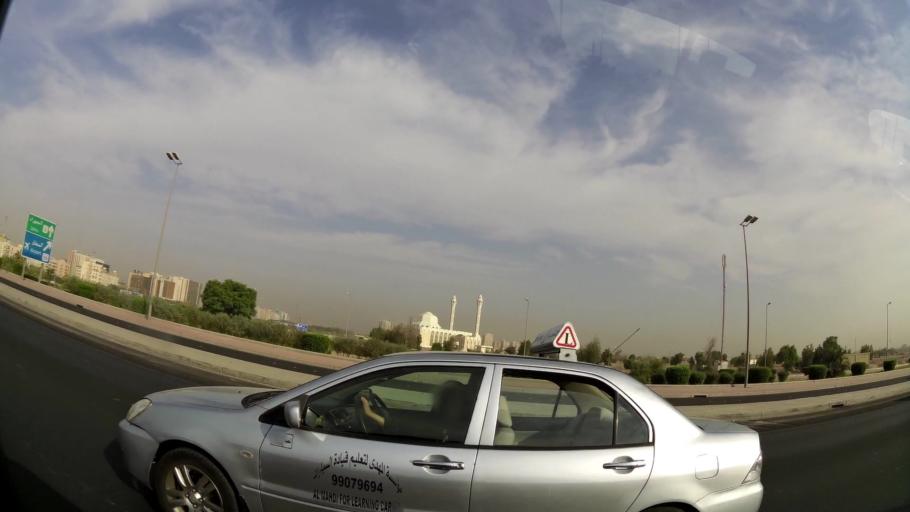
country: KW
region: Al Farwaniyah
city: Janub as Surrah
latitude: 29.2658
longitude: 47.9723
